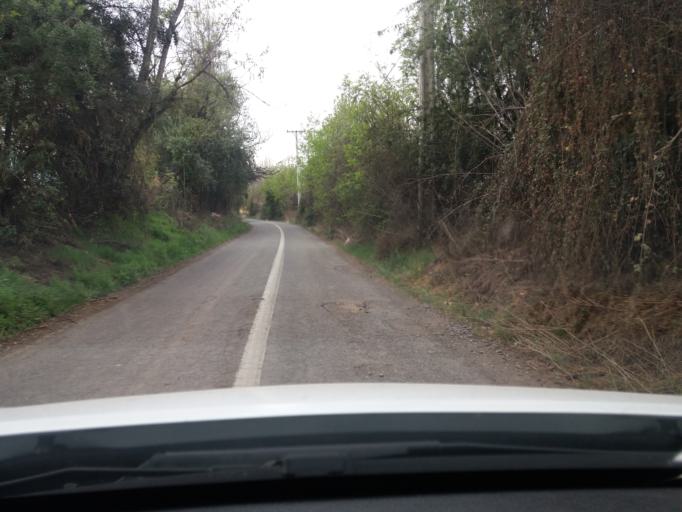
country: CL
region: Valparaiso
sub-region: Provincia de Los Andes
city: Los Andes
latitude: -32.8251
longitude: -70.6392
